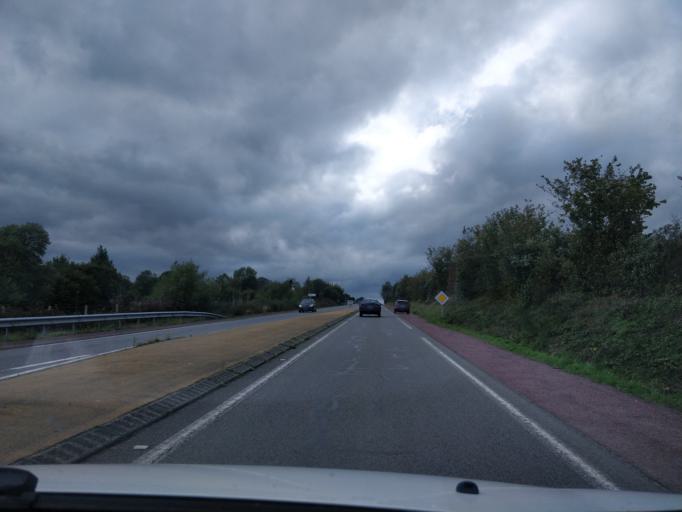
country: FR
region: Lower Normandy
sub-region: Departement du Calvados
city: Saint-Sever-Calvados
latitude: 48.8380
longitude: -1.0274
